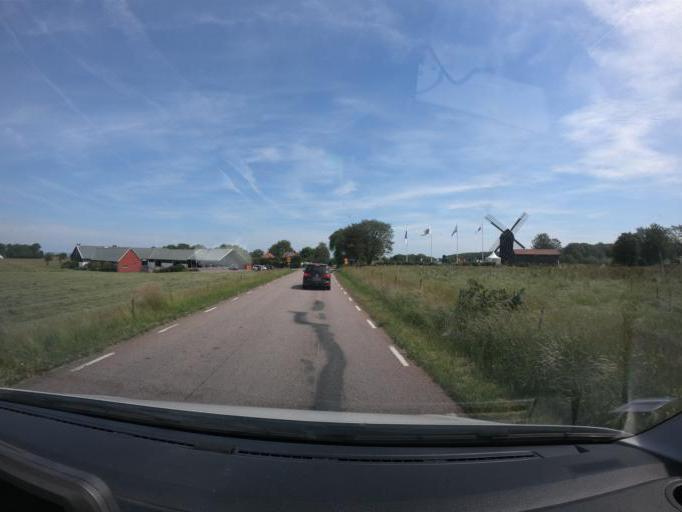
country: SE
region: Skane
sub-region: Bastads Kommun
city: Bastad
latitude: 56.4273
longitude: 12.7872
